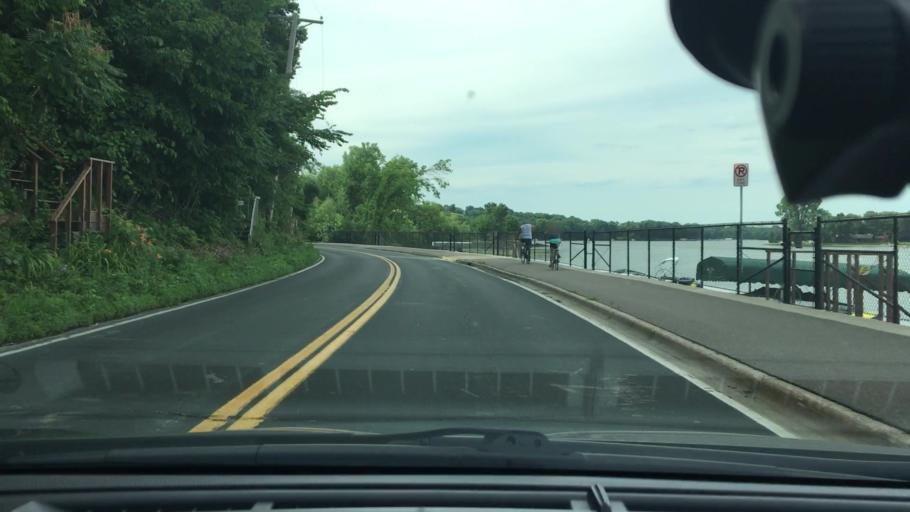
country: US
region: Minnesota
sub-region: Hennepin County
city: Plymouth
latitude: 44.9975
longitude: -93.4277
